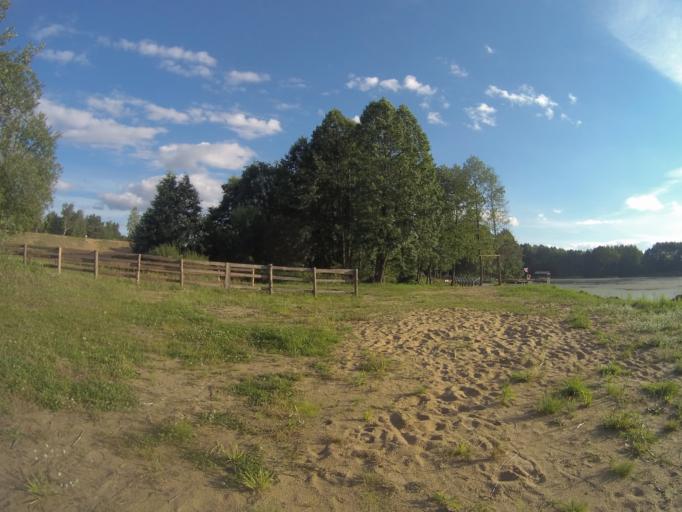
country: RU
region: Vladimir
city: Kommunar
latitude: 56.1019
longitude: 40.4353
